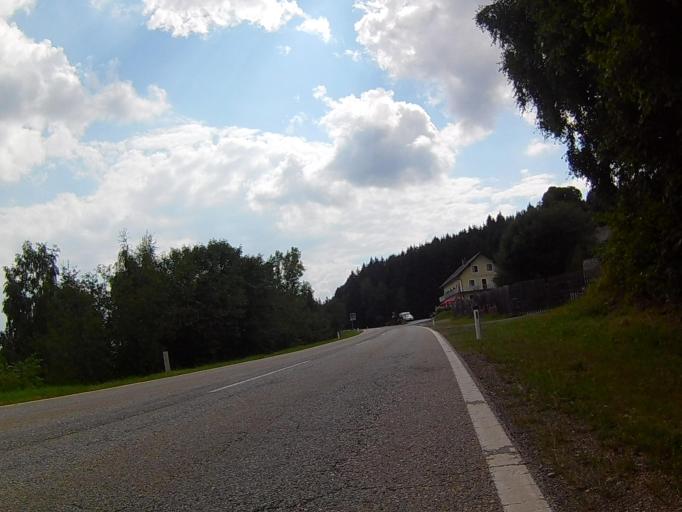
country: AT
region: Styria
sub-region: Politischer Bezirk Deutschlandsberg
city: Soboth
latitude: 46.6865
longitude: 15.1003
